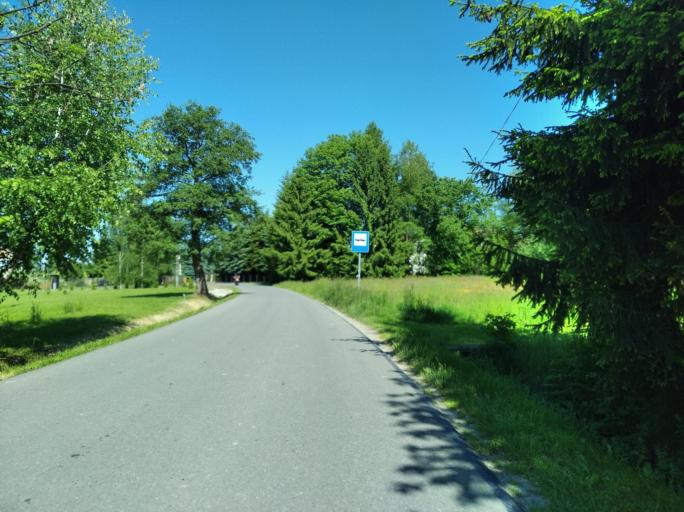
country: PL
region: Subcarpathian Voivodeship
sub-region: Powiat krosnienski
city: Korczyna
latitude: 49.7212
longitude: 21.7885
